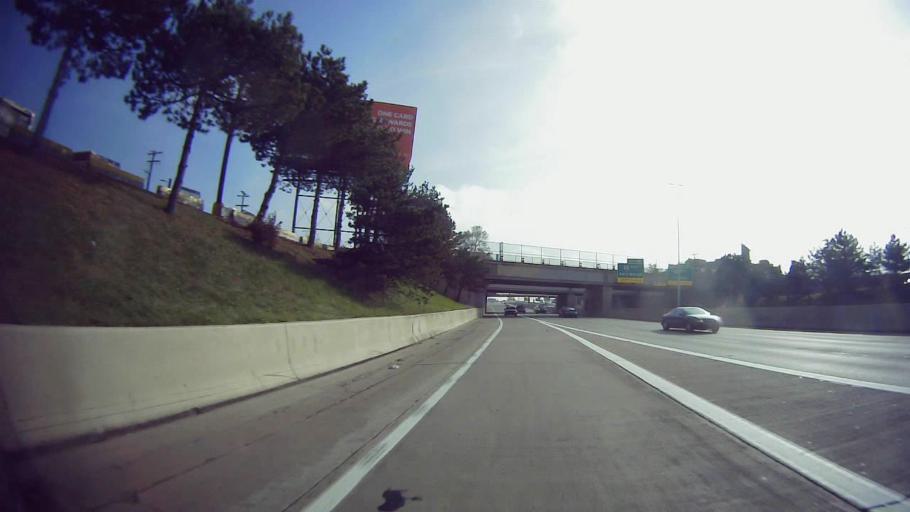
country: US
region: Michigan
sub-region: Wayne County
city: Hamtramck
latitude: 42.3648
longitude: -83.0798
